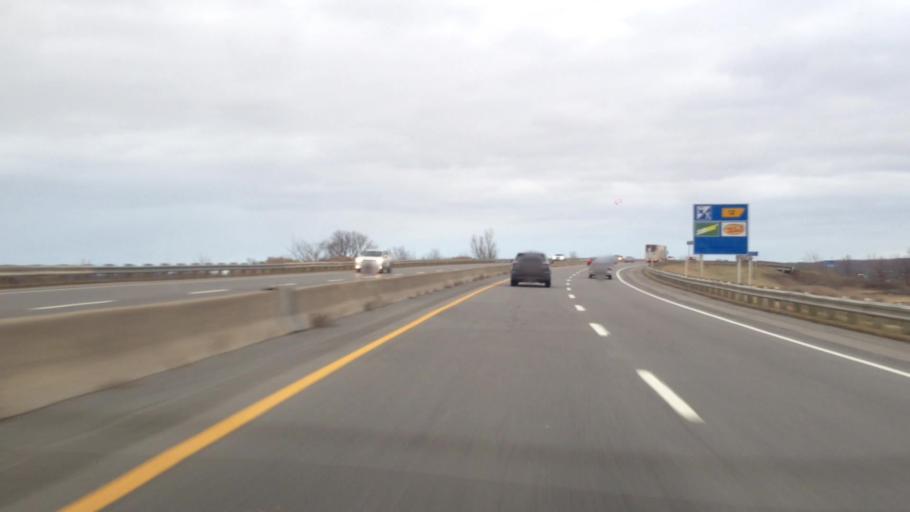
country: CA
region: Quebec
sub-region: Monteregie
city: Rigaud
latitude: 45.4841
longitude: -74.2920
